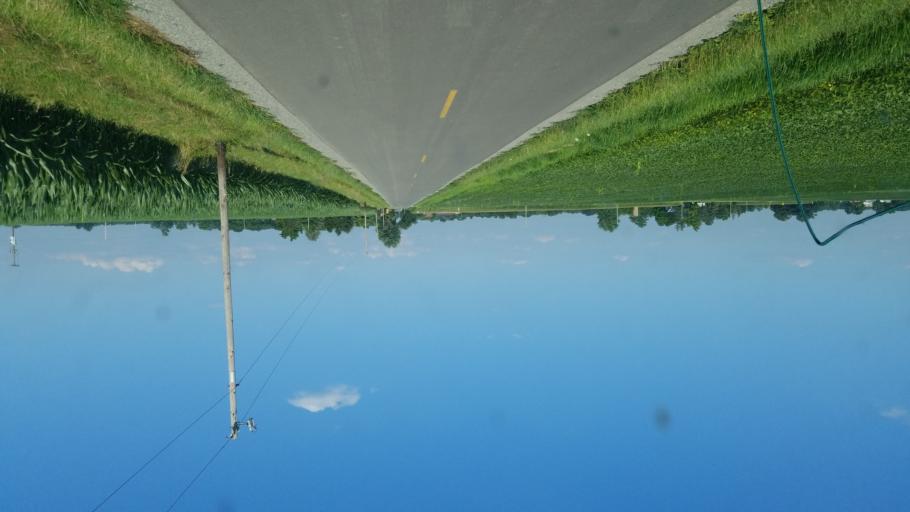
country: US
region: Ohio
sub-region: Wyandot County
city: Upper Sandusky
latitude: 40.7888
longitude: -83.2972
